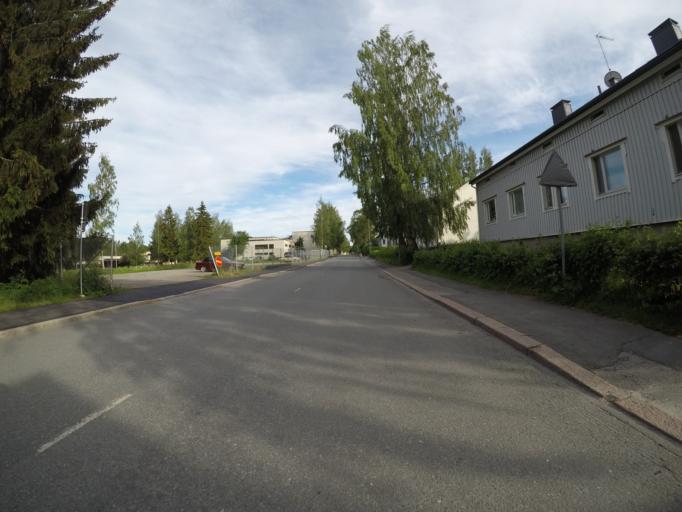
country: FI
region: Haeme
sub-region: Haemeenlinna
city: Haemeenlinna
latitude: 60.9970
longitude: 24.4487
